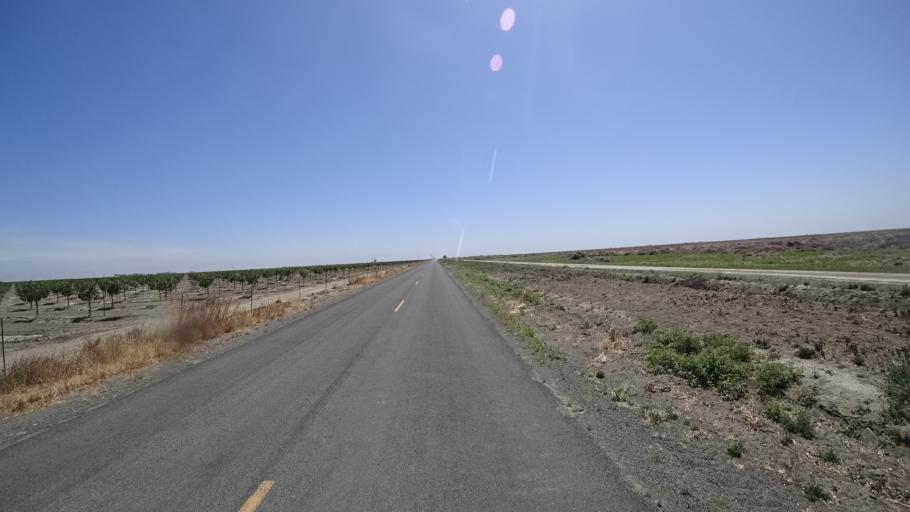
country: US
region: California
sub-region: Kings County
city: Stratford
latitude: 36.1892
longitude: -119.7346
